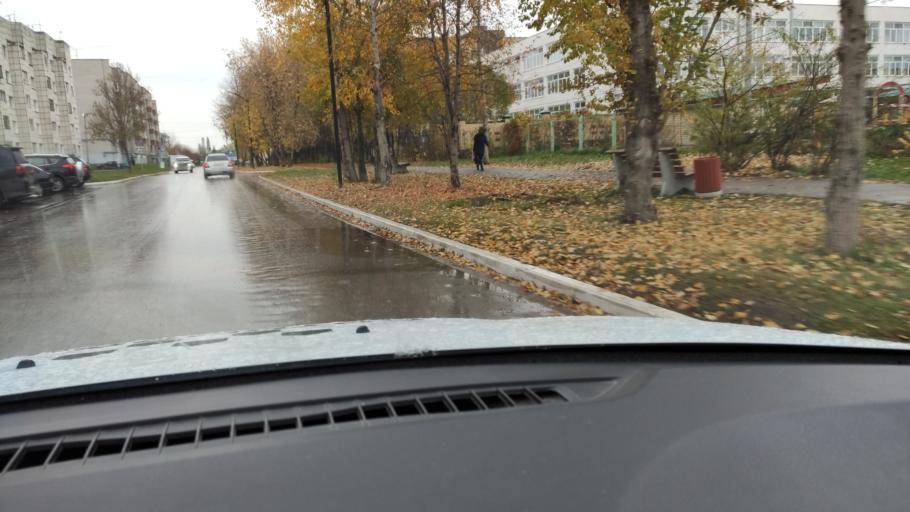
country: RU
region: Perm
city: Kondratovo
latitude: 57.9787
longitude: 56.1032
